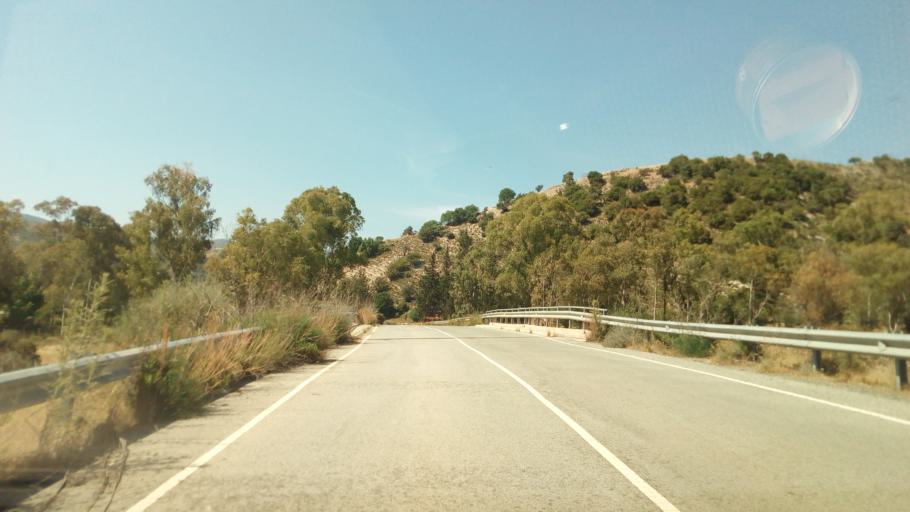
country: CY
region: Limassol
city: Pachna
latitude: 34.8100
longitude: 32.7126
